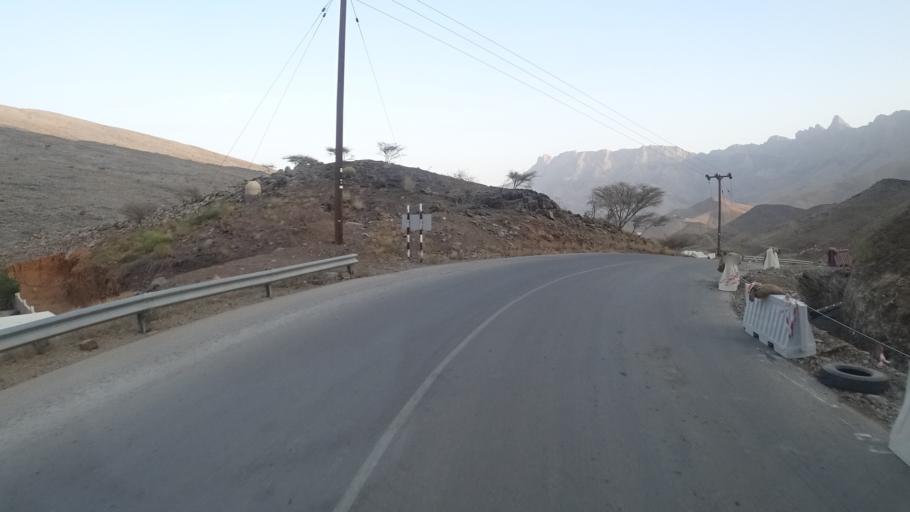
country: OM
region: Muhafazat ad Dakhiliyah
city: Bahla'
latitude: 23.1905
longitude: 57.1380
